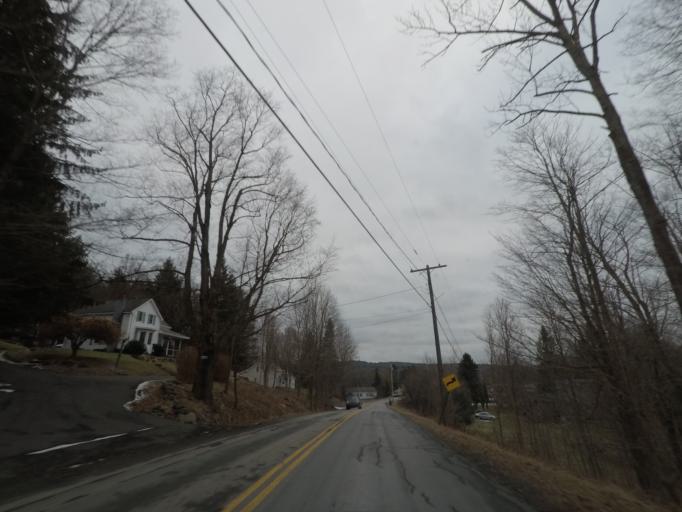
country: US
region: New York
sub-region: Rensselaer County
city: Poestenkill
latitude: 42.7667
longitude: -73.4512
